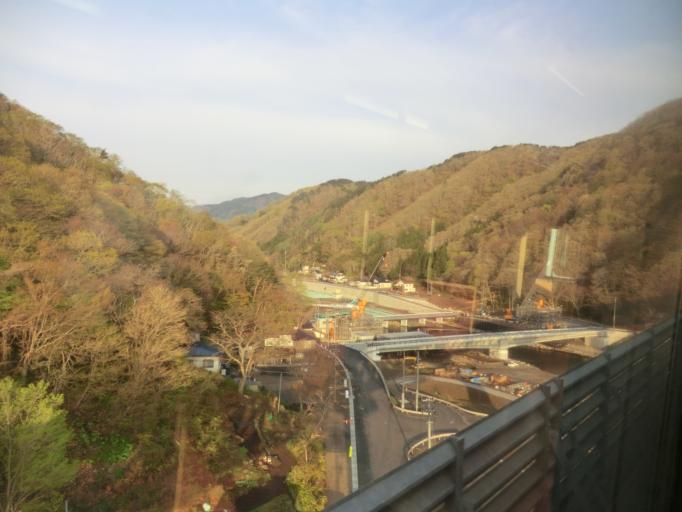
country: JP
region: Iwate
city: Miyako
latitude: 40.0551
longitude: 141.8498
